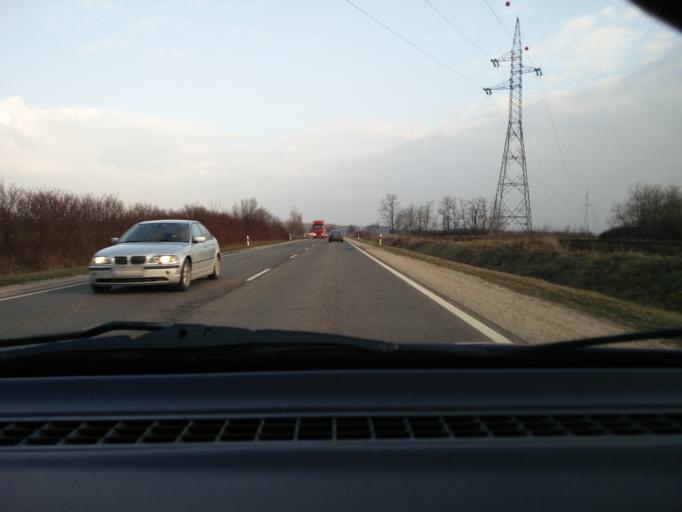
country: HU
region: Pest
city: Pilis
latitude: 47.2578
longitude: 19.5442
